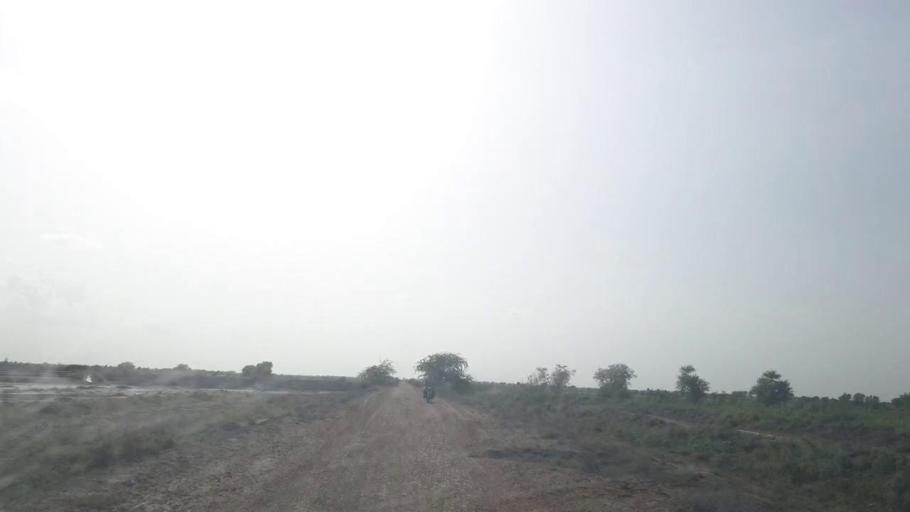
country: PK
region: Sindh
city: Tando Bago
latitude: 24.8121
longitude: 69.1563
